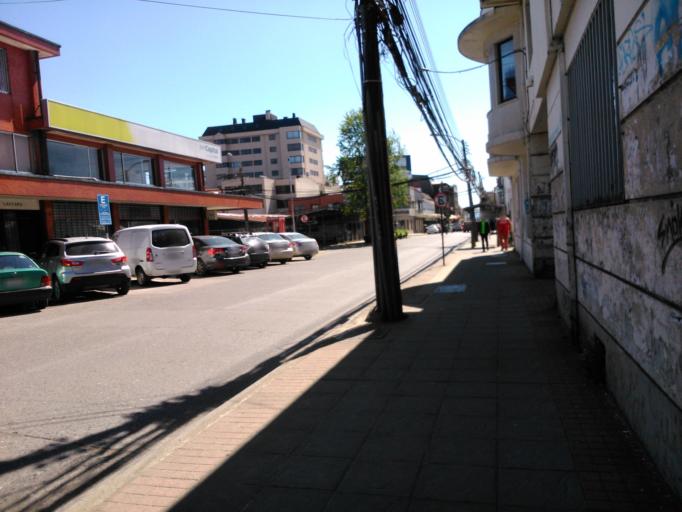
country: CL
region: Los Rios
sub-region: Provincia de Valdivia
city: Valdivia
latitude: -39.8166
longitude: -73.2468
